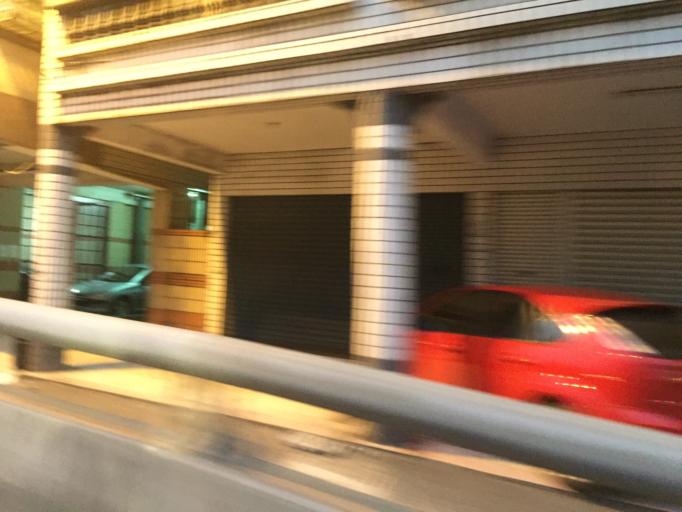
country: TW
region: Taiwan
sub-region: Yilan
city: Yilan
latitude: 24.7567
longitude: 121.7466
